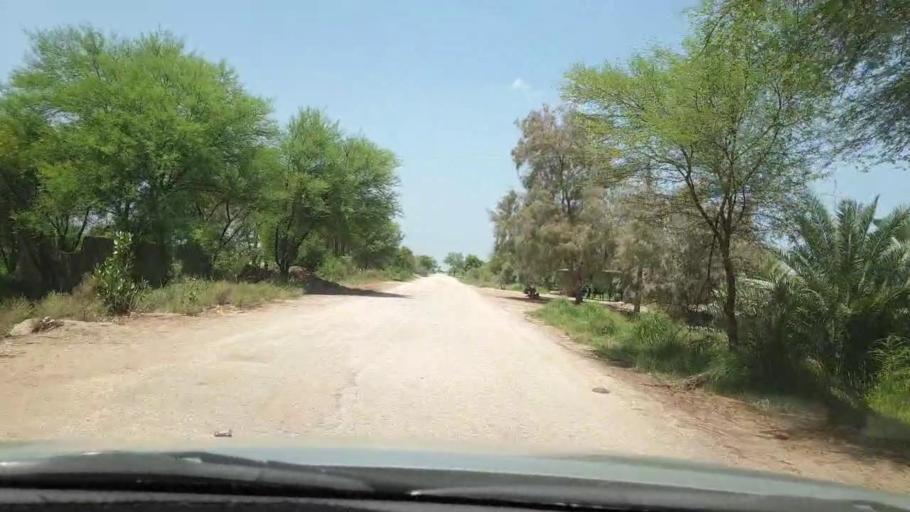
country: PK
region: Sindh
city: Pano Aqil
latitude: 27.7093
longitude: 69.2164
